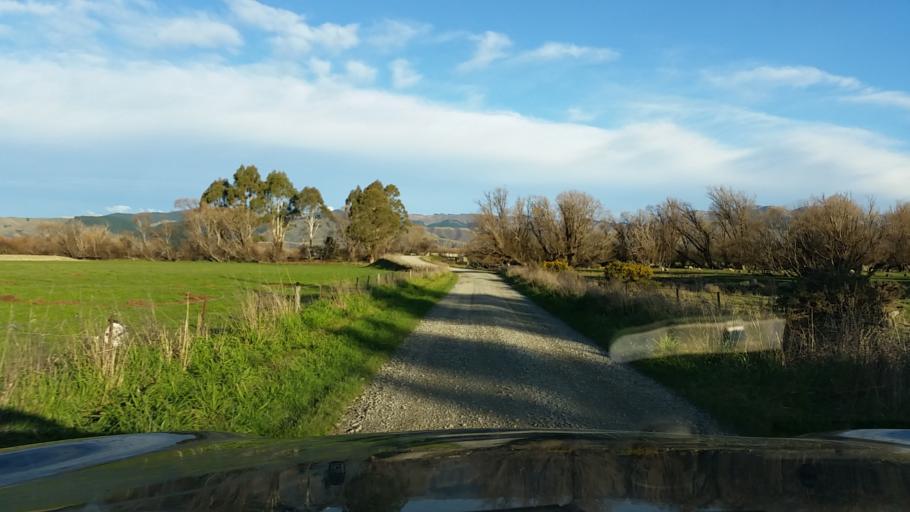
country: NZ
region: Nelson
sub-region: Nelson City
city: Nelson
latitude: -41.5419
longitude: 173.4966
